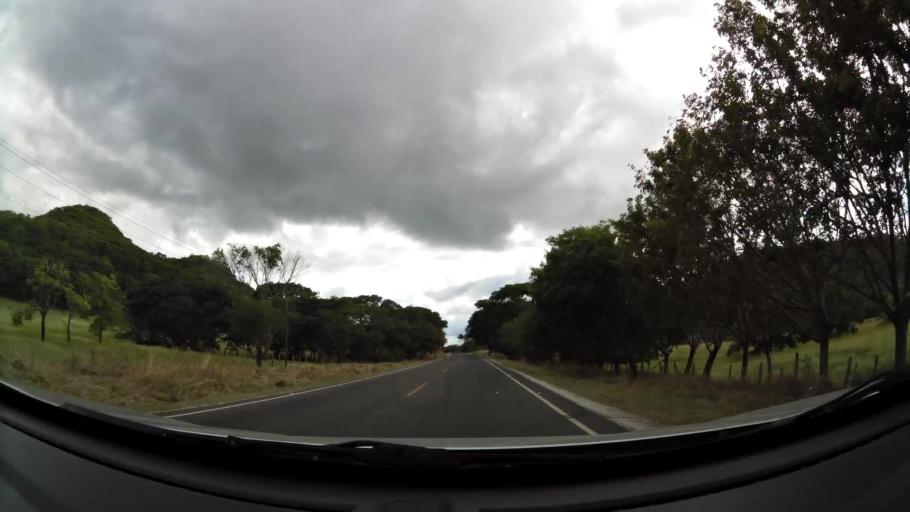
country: CR
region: Guanacaste
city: Nandayure
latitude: 10.2281
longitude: -85.2178
